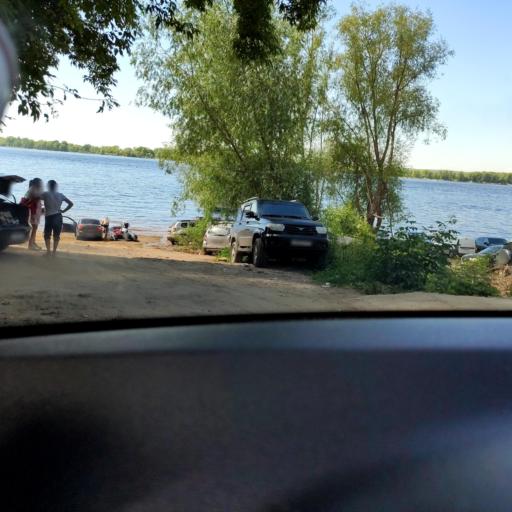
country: RU
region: Samara
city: Samara
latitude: 53.2437
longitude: 50.1696
